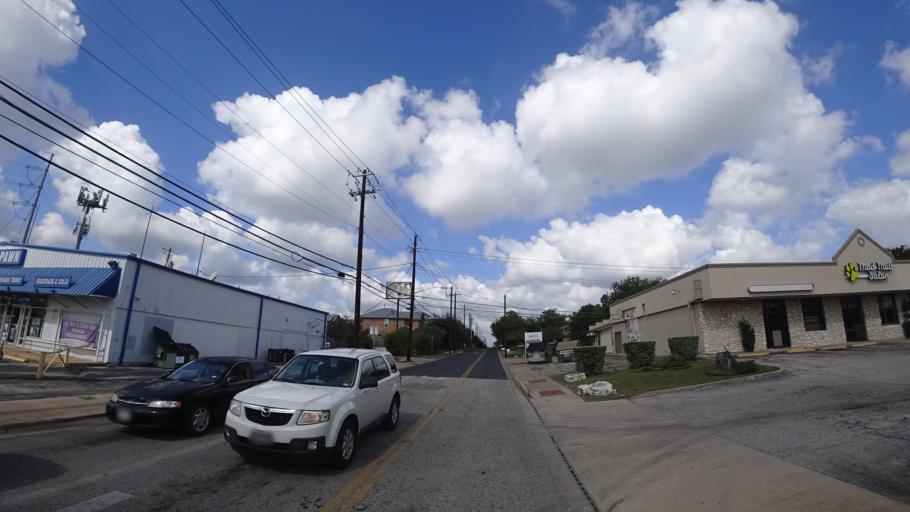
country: US
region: Texas
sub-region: Travis County
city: Austin
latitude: 30.3441
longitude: -97.7151
